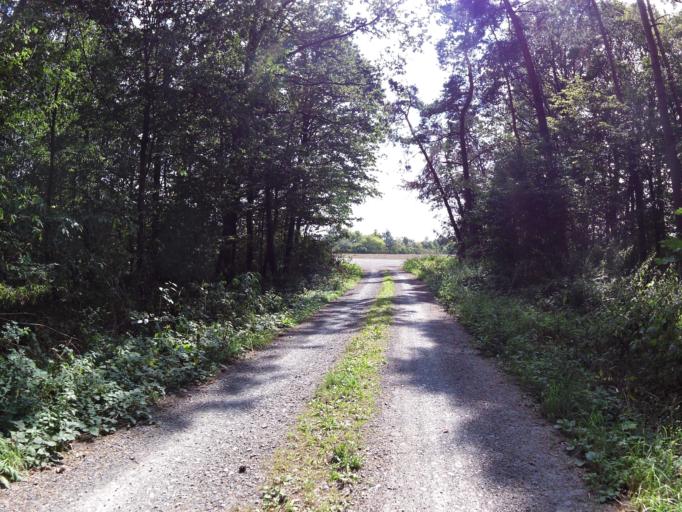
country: DE
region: Bavaria
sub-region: Regierungsbezirk Unterfranken
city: Kleinrinderfeld
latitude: 49.7080
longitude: 9.8020
